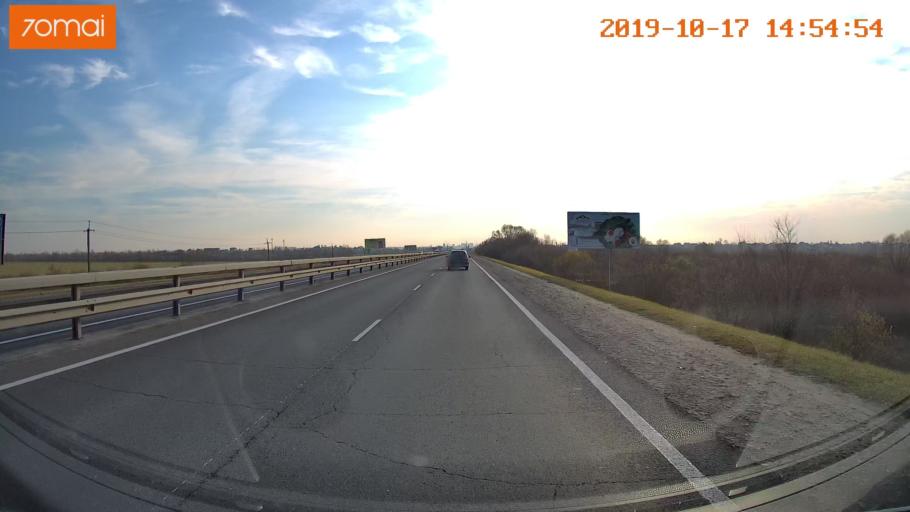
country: RU
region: Rjazan
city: Polyany
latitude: 54.6752
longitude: 39.8287
